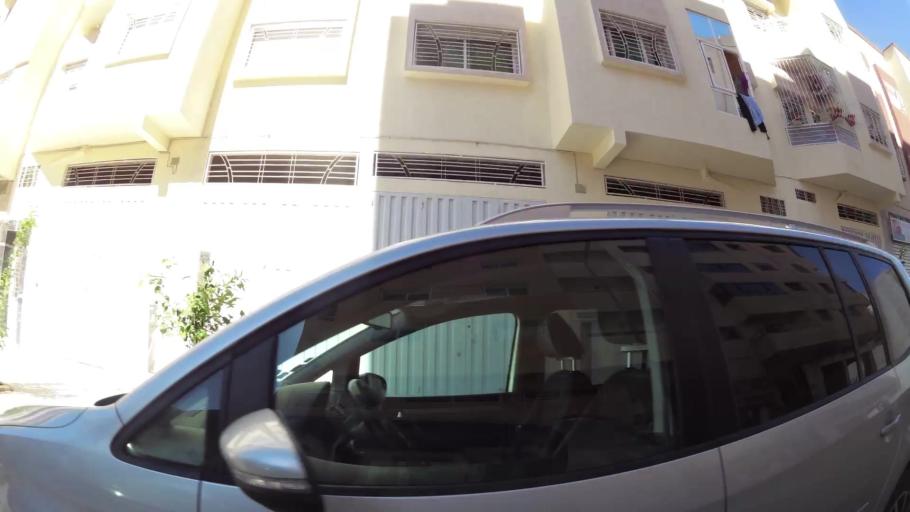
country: MA
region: Fes-Boulemane
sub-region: Fes
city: Fes
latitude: 34.0001
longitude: -5.0098
